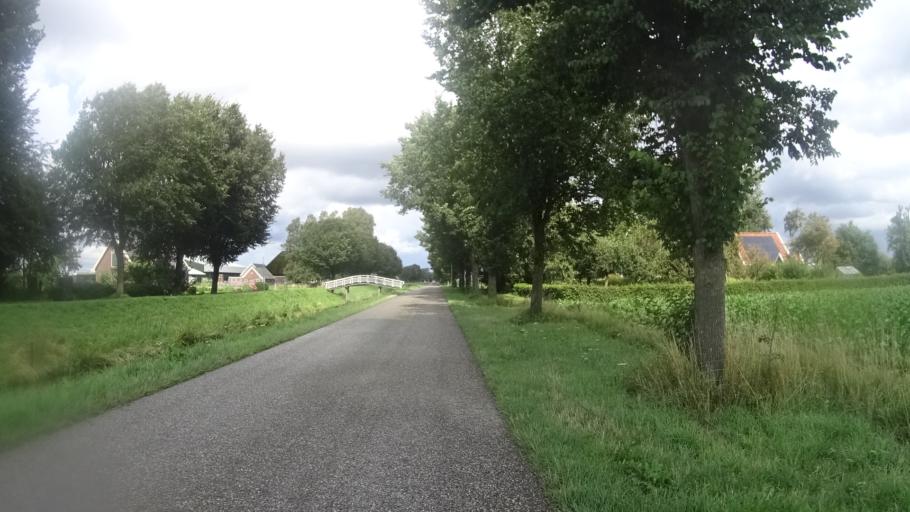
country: NL
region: North Holland
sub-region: Gemeente Schagen
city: Schagen
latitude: 52.8325
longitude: 4.8409
